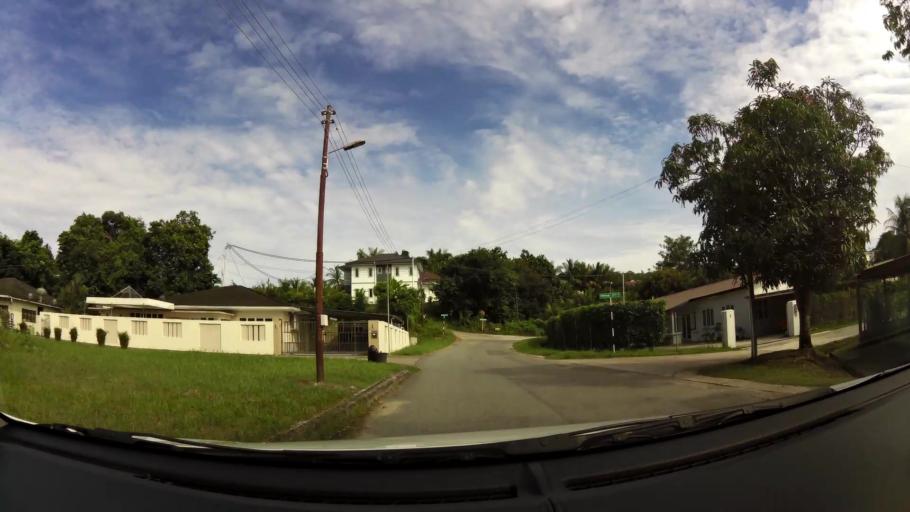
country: BN
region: Brunei and Muara
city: Bandar Seri Begawan
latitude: 4.8978
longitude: 114.9709
